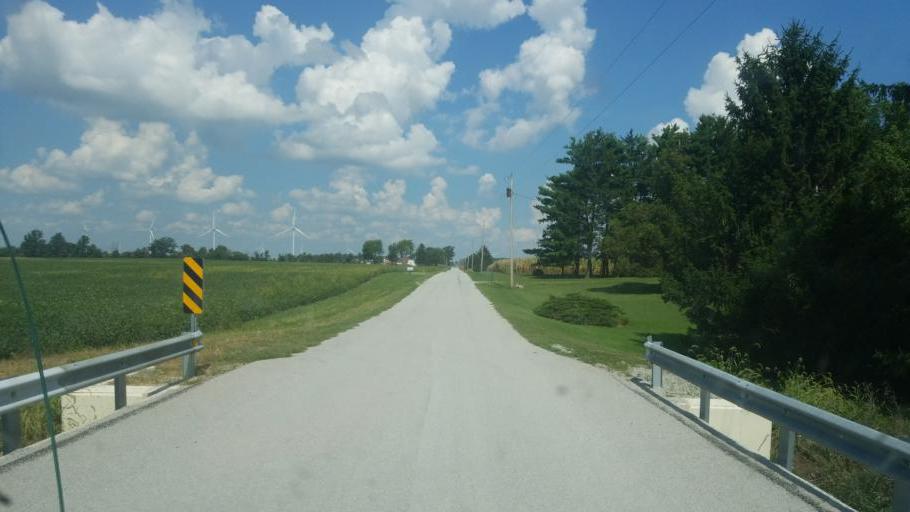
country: US
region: Ohio
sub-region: Hardin County
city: Ada
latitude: 40.7489
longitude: -83.7097
